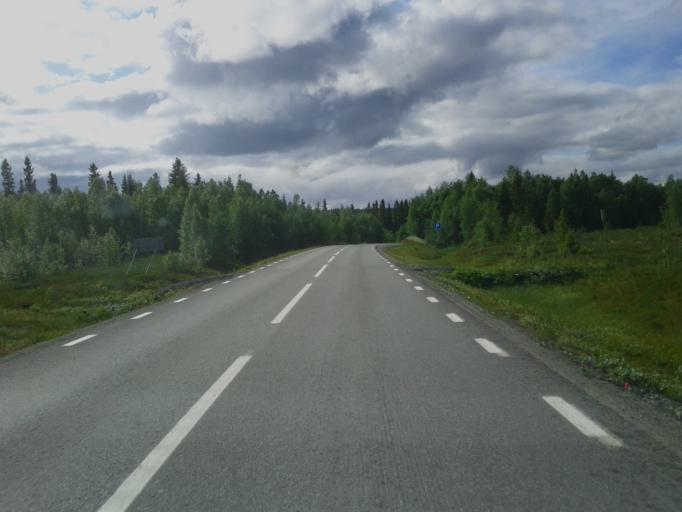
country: NO
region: Nordland
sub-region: Rana
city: Mo i Rana
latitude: 65.7122
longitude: 15.2228
